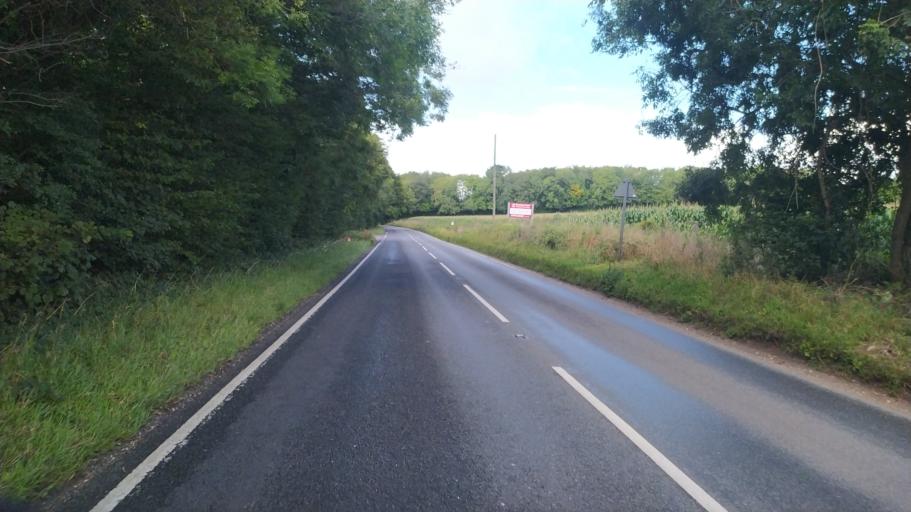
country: GB
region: England
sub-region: Dorset
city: Blandford Forum
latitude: 50.8585
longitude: -2.1239
